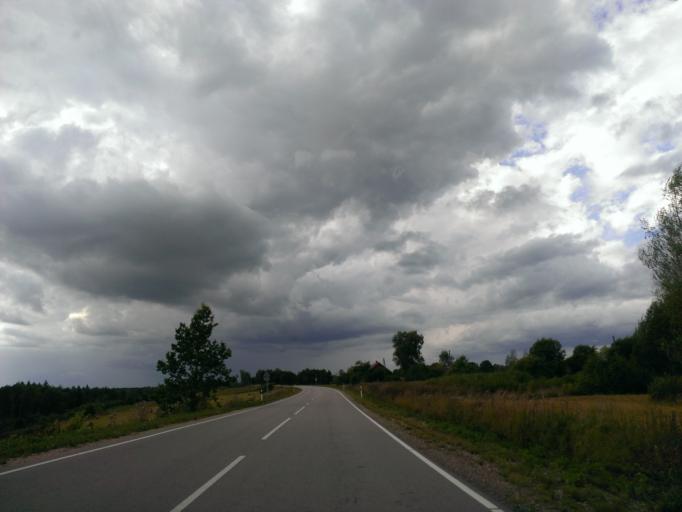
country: LV
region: Malpils
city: Malpils
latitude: 56.8949
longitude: 25.1515
